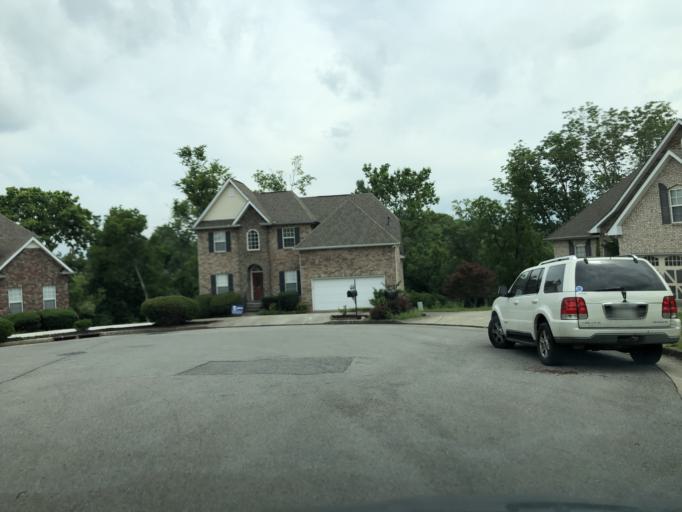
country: US
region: Tennessee
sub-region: Davidson County
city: Goodlettsville
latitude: 36.2814
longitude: -86.7421
